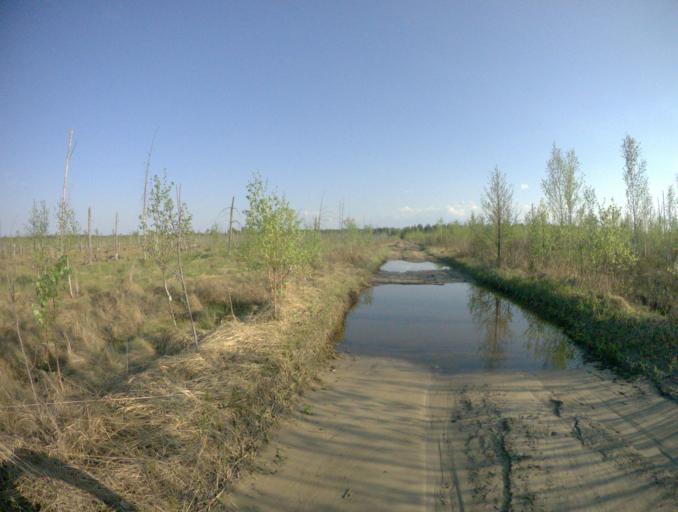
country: RU
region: Vladimir
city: Vyazniki
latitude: 56.3843
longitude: 42.1727
